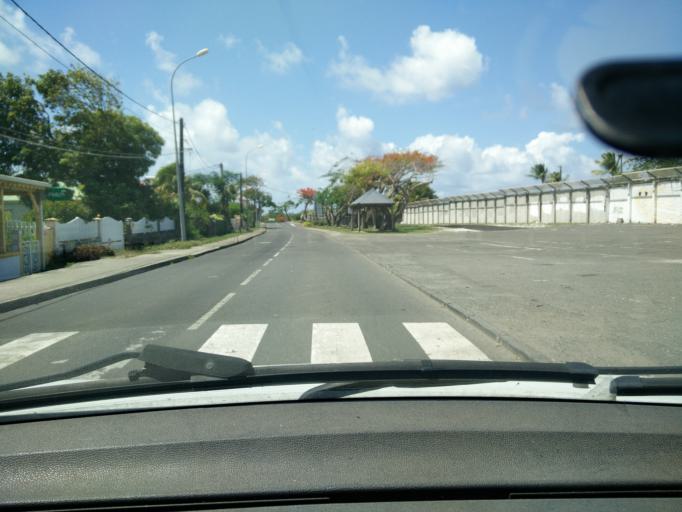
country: GP
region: Guadeloupe
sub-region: Guadeloupe
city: Le Moule
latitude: 16.3204
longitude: -61.3437
